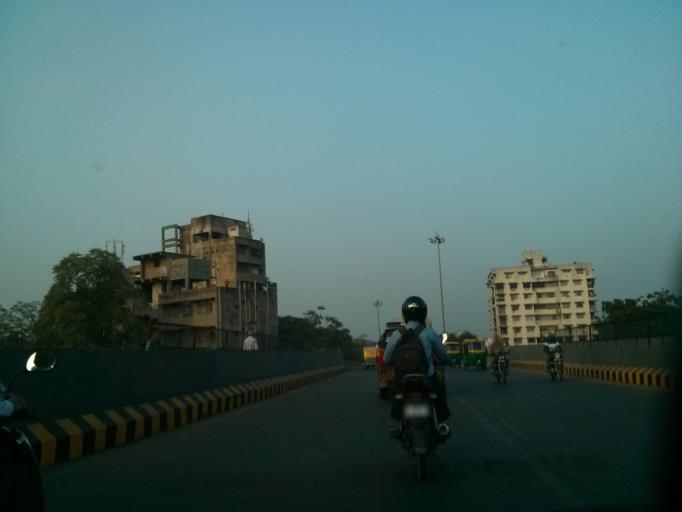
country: IN
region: Gujarat
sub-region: Ahmadabad
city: Ahmedabad
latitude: 23.0494
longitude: 72.5932
